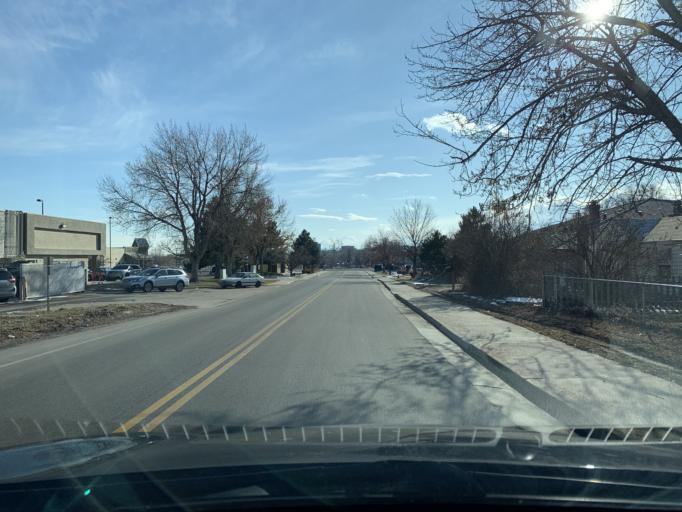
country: US
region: Colorado
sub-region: Jefferson County
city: Applewood
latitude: 39.7420
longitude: -105.1260
